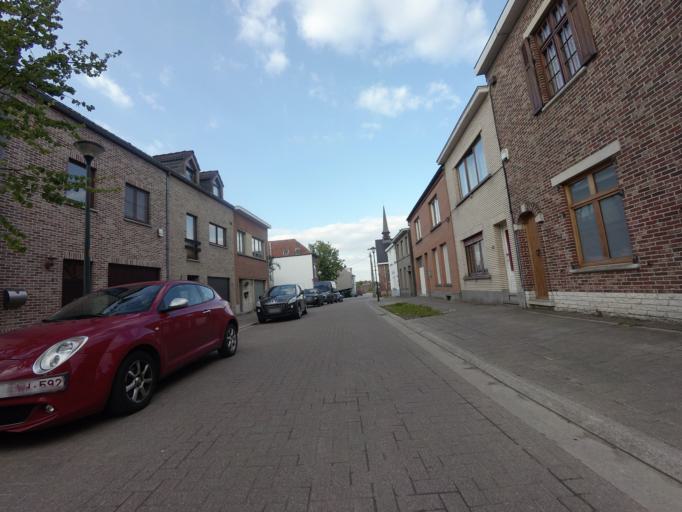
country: BE
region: Flanders
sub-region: Provincie Vlaams-Brabant
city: Grimbergen
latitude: 50.9061
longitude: 4.3800
